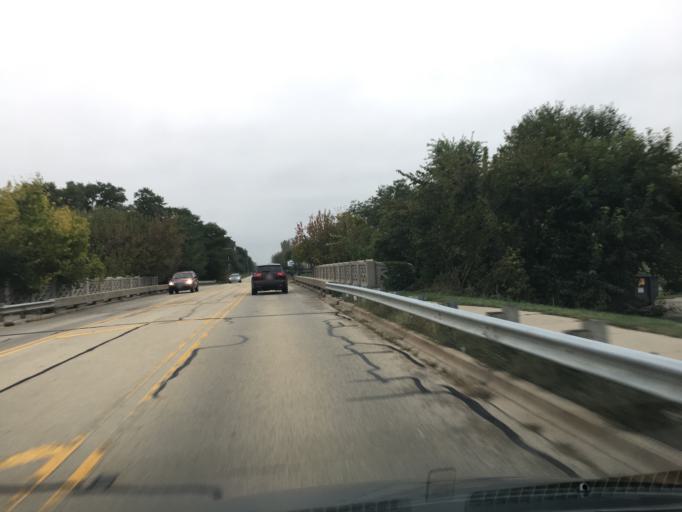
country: US
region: Illinois
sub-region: Will County
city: Plainfield
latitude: 41.6465
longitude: -88.1647
